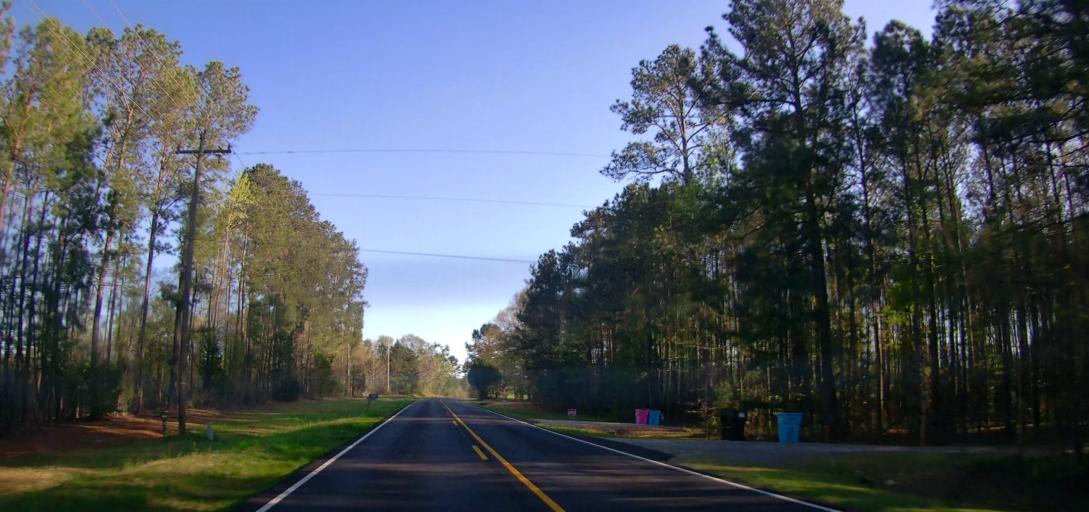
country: US
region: Georgia
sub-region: Butts County
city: Jackson
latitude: 33.3455
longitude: -83.9098
